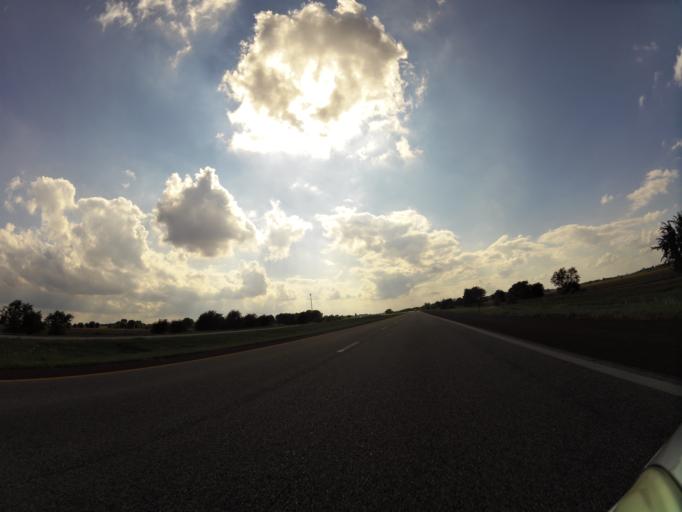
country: US
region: Kansas
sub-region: Reno County
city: Haven
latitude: 37.8928
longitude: -97.7608
